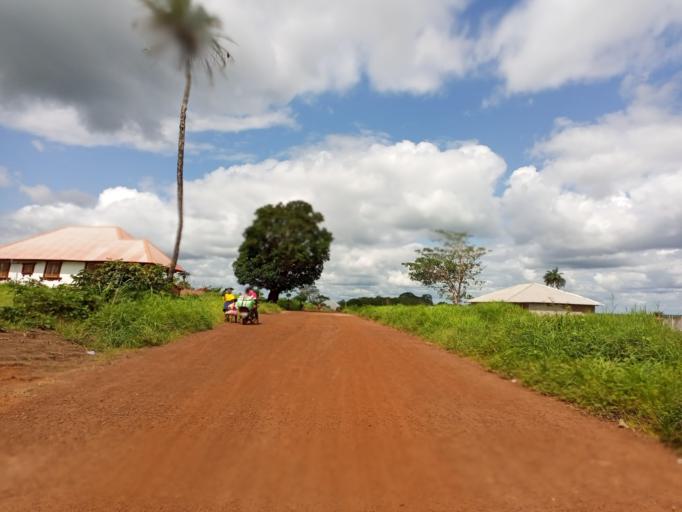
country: SL
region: Northern Province
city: Kamakwie
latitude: 9.5059
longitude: -12.2319
